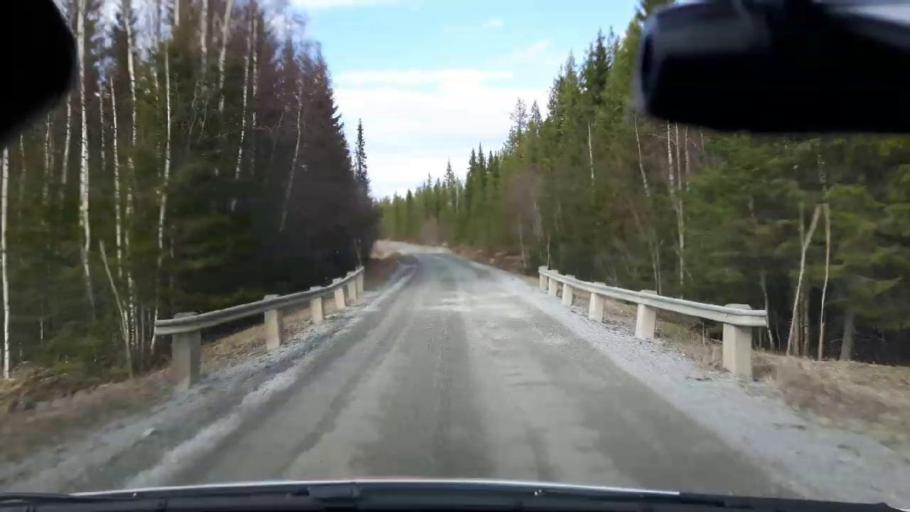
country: SE
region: Jaemtland
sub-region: Bergs Kommun
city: Hoverberg
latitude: 62.7654
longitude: 14.6816
